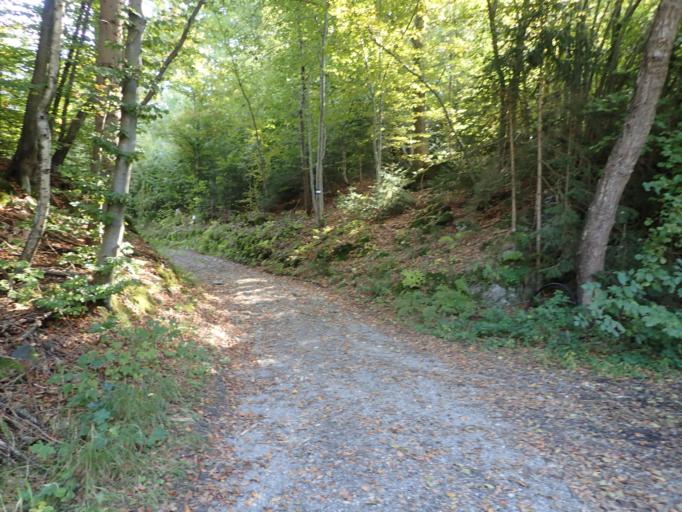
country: AT
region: Carinthia
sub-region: Politischer Bezirk Klagenfurt Land
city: Maria Worth
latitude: 46.6400
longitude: 14.1300
